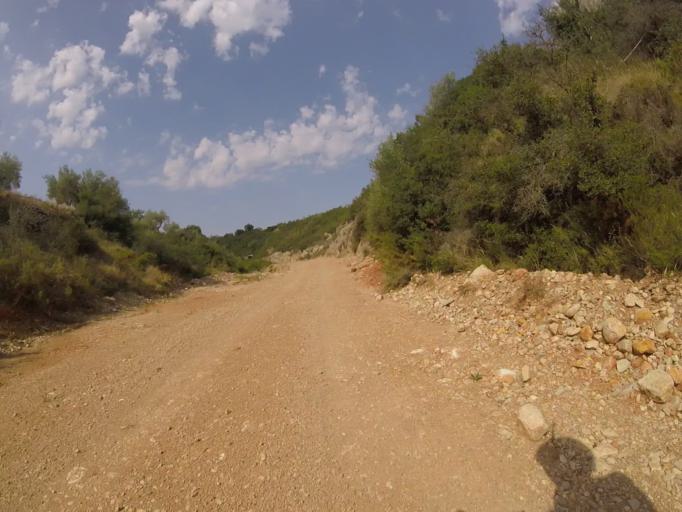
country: ES
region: Valencia
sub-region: Provincia de Castello
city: Alcala de Xivert
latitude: 40.3335
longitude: 0.1944
